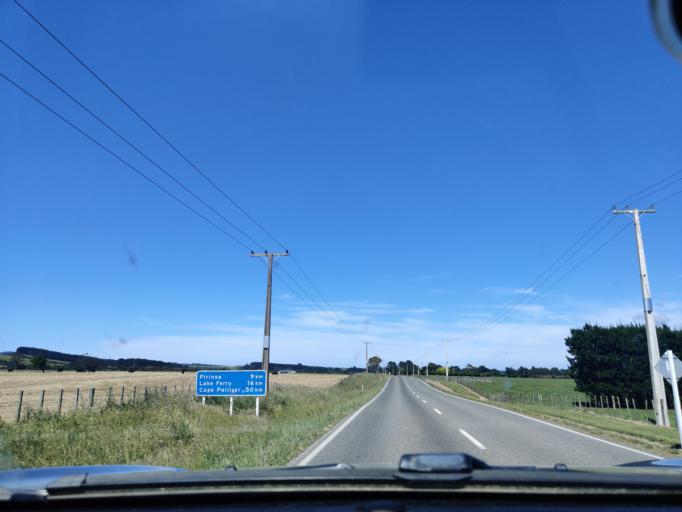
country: NZ
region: Wellington
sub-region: South Wairarapa District
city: Waipawa
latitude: -41.3071
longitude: 175.2722
